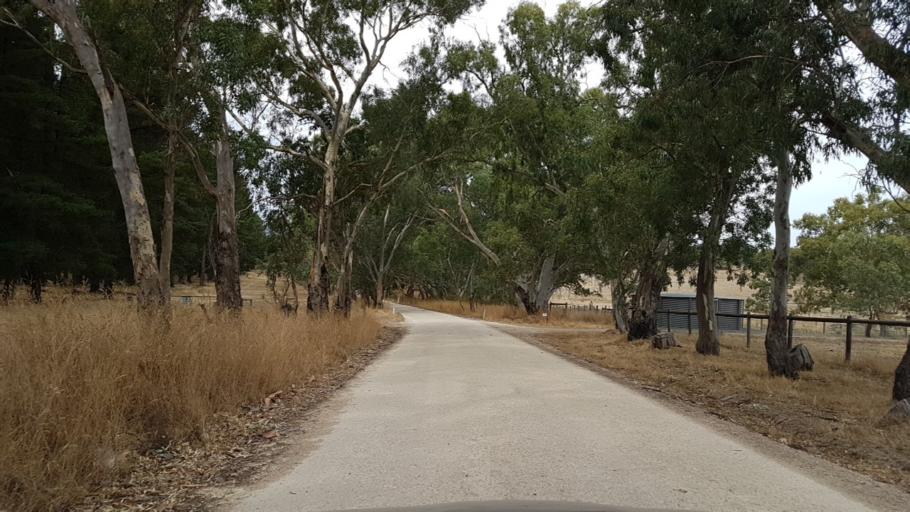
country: AU
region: South Australia
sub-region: Adelaide Hills
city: Birdwood
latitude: -34.7851
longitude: 138.9815
